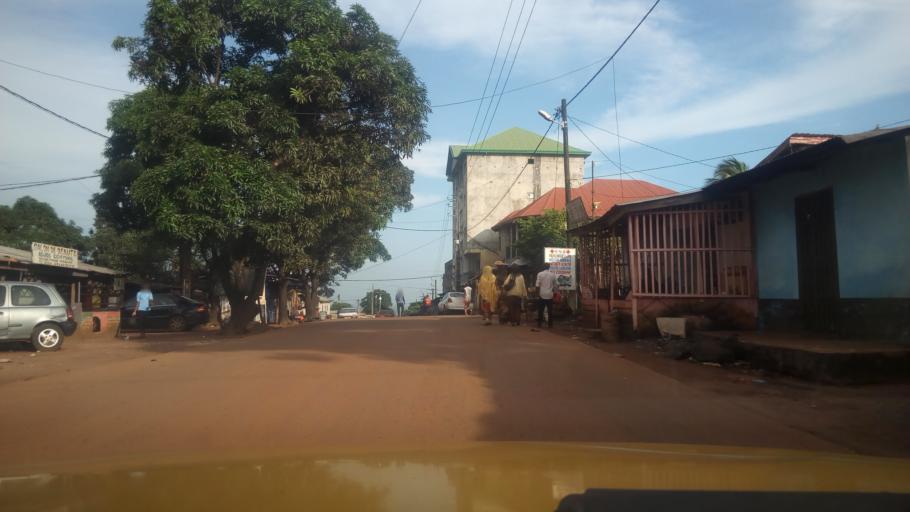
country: GN
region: Conakry
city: Conakry
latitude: 9.6167
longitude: -13.6081
